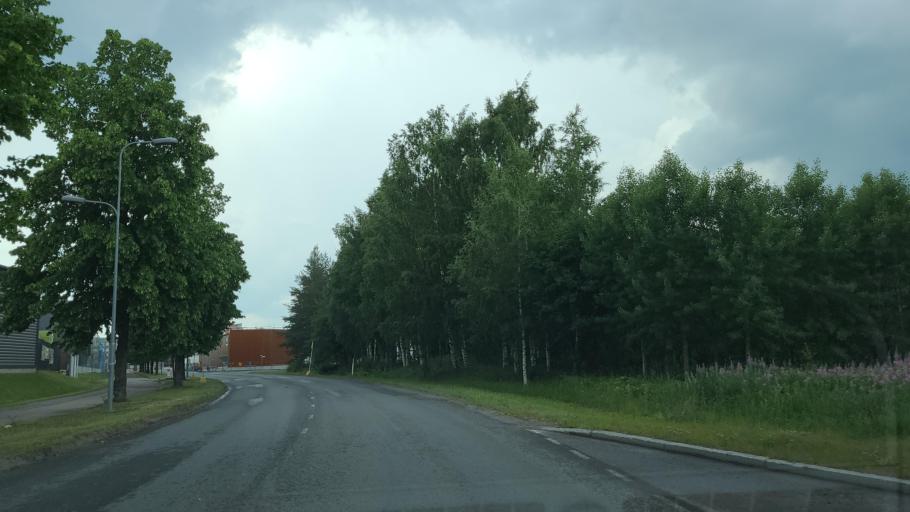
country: FI
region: Ostrobothnia
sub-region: Vaasa
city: Vaasa
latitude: 63.0975
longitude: 21.6386
